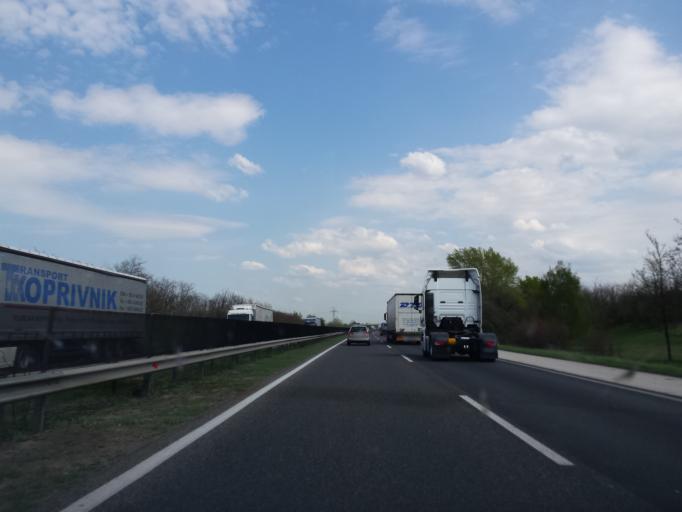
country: HU
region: Gyor-Moson-Sopron
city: Bony
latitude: 47.6843
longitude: 17.8776
